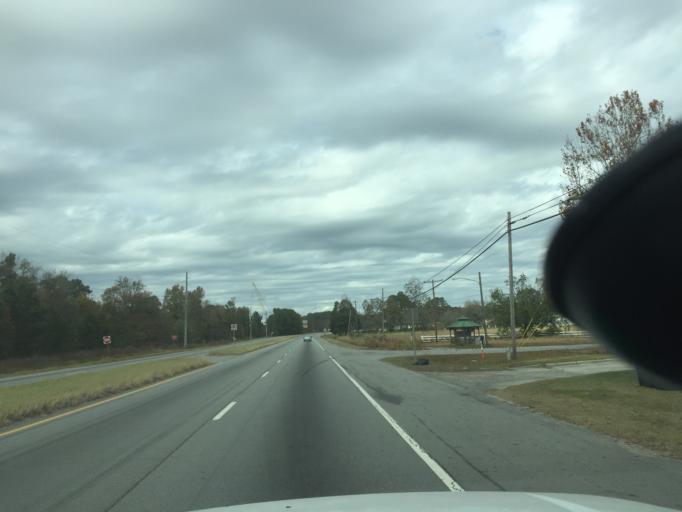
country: US
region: Georgia
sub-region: Chatham County
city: Port Wentworth
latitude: 32.1667
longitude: -81.1855
